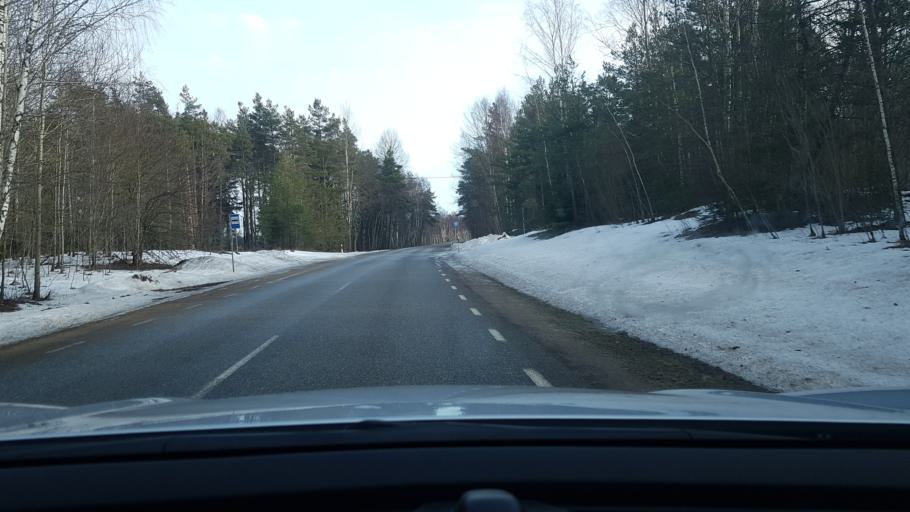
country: EE
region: Saare
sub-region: Kuressaare linn
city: Kuressaare
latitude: 58.4244
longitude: 22.6718
